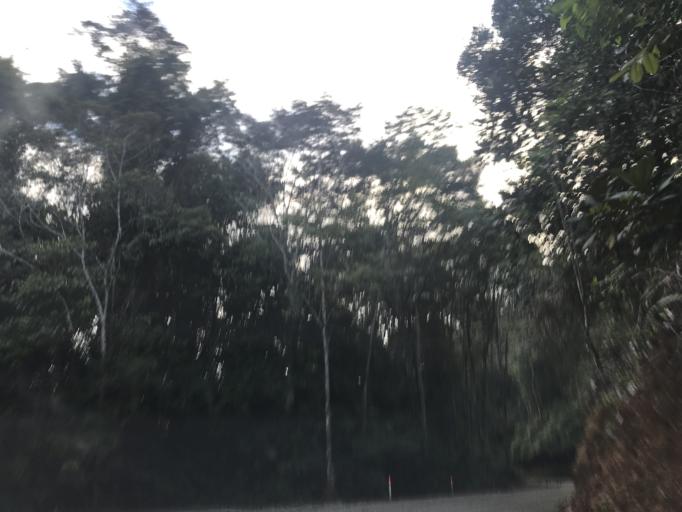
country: BR
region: Bahia
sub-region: Gandu
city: Gandu
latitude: -13.9057
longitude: -39.4607
